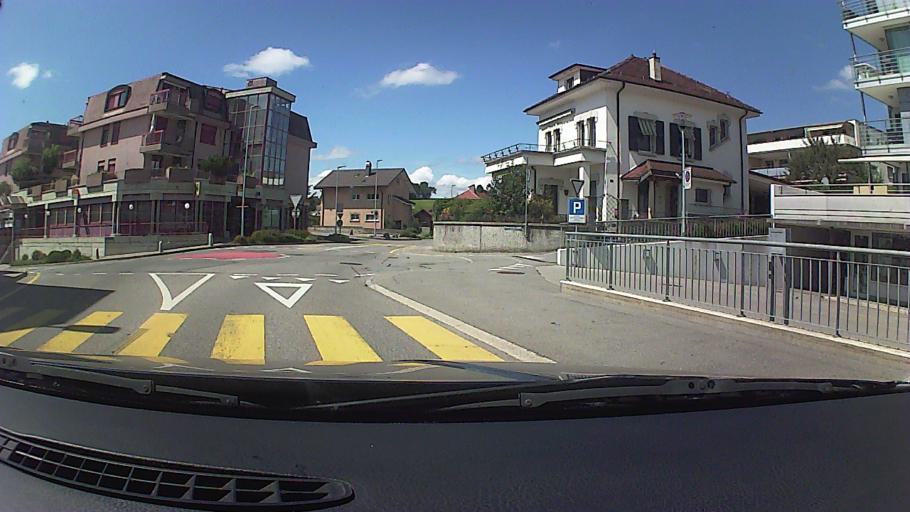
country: CH
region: Fribourg
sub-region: Veveyse District
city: Chatel-Saint-Denis
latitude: 46.5276
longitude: 6.8989
